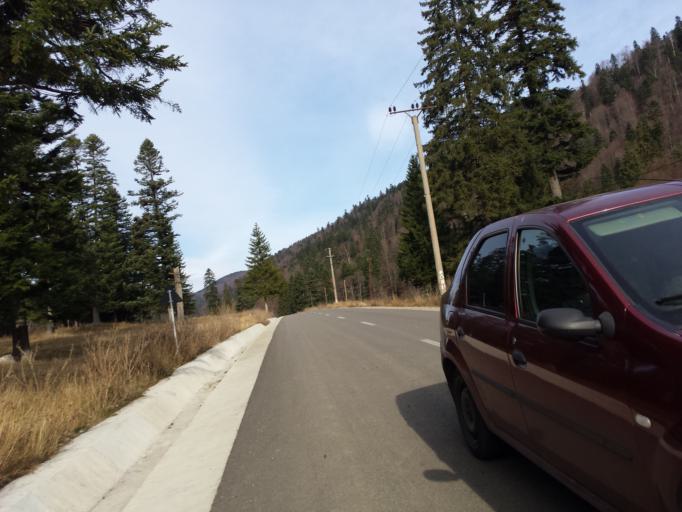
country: RO
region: Prahova
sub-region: Oras Azuga
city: Azuga
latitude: 45.4359
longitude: 25.5295
